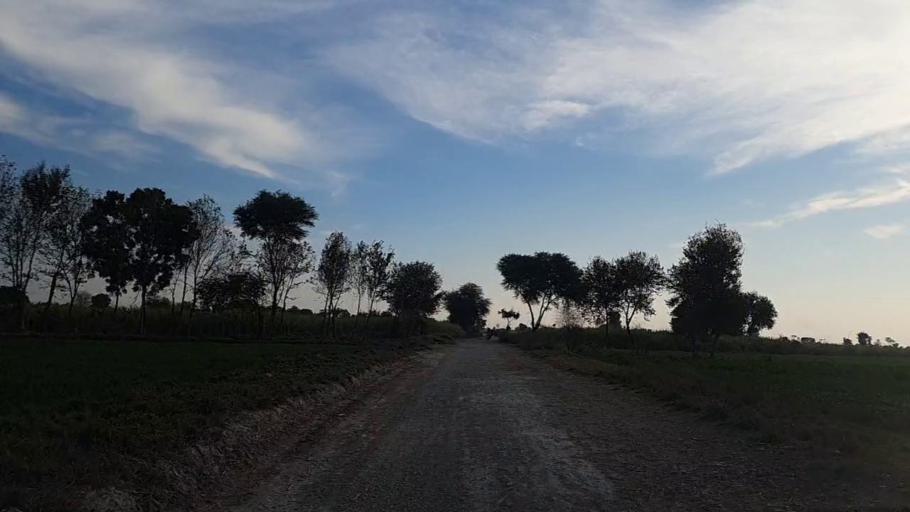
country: PK
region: Sindh
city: Bandhi
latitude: 26.5556
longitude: 68.2809
